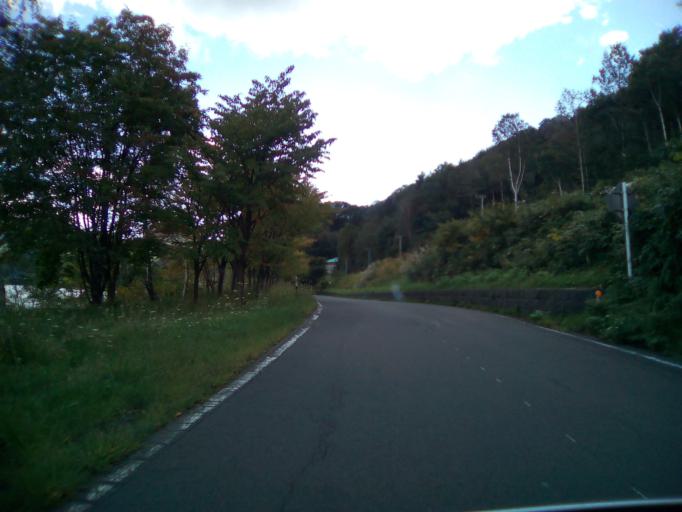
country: JP
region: Hokkaido
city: Date
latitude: 42.5824
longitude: 140.7956
